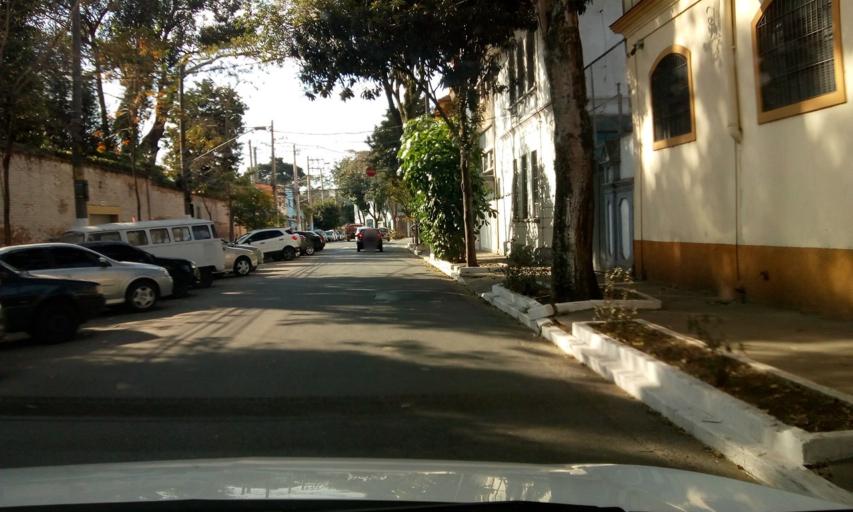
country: BR
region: Sao Paulo
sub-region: Sao Paulo
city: Sao Paulo
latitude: -23.5302
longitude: -46.6292
